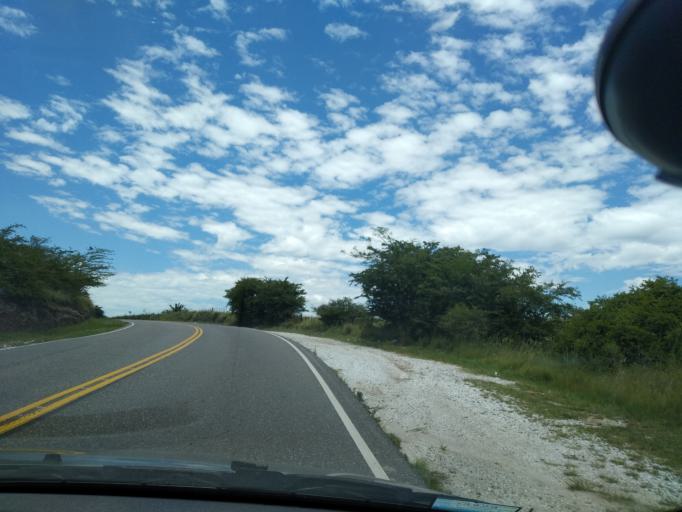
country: AR
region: Cordoba
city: Cuesta Blanca
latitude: -31.5990
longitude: -64.5635
